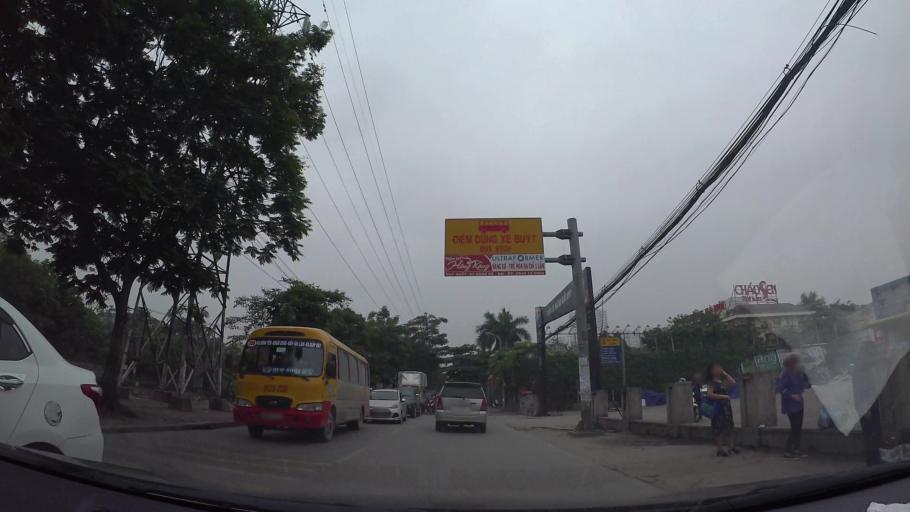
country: VN
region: Ha Noi
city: Hai BaTrung
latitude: 20.9847
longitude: 105.8638
